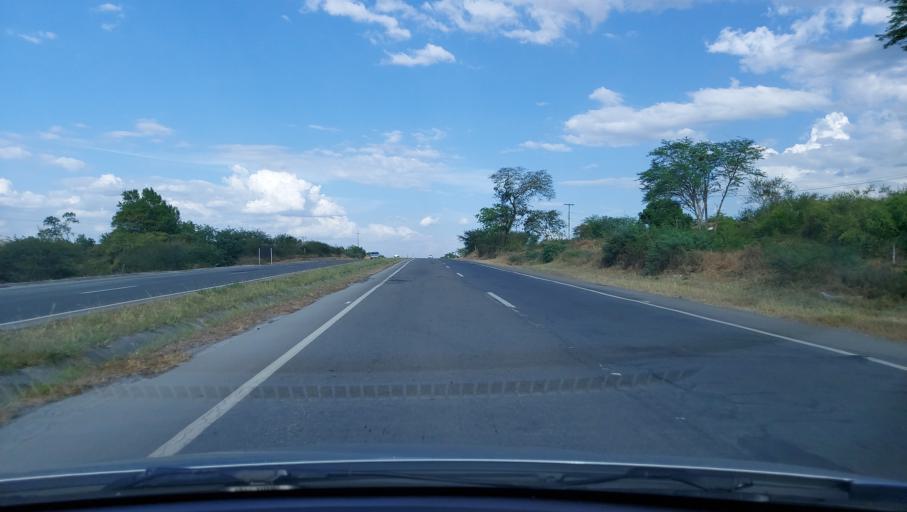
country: BR
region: Bahia
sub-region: Santo Estevao
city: Santo Estevao
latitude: -12.5082
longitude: -39.3669
